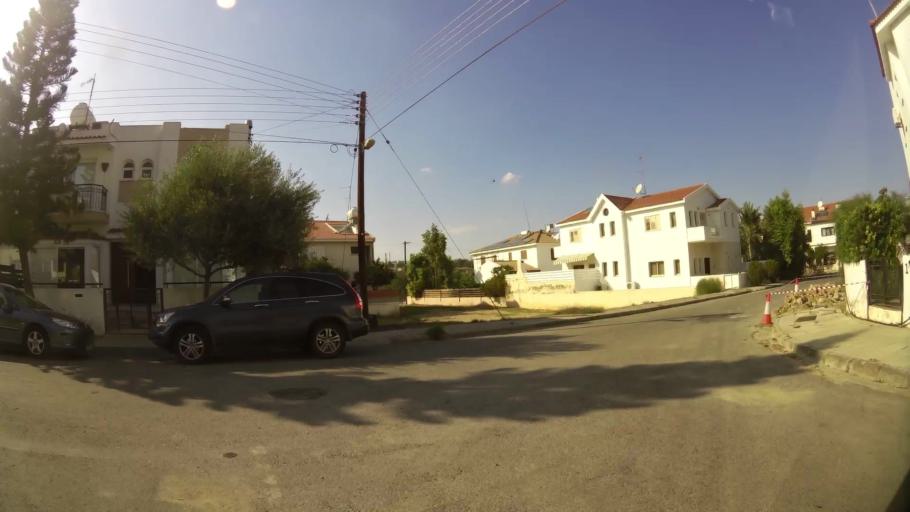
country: CY
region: Lefkosia
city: Nicosia
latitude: 35.1487
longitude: 33.3055
